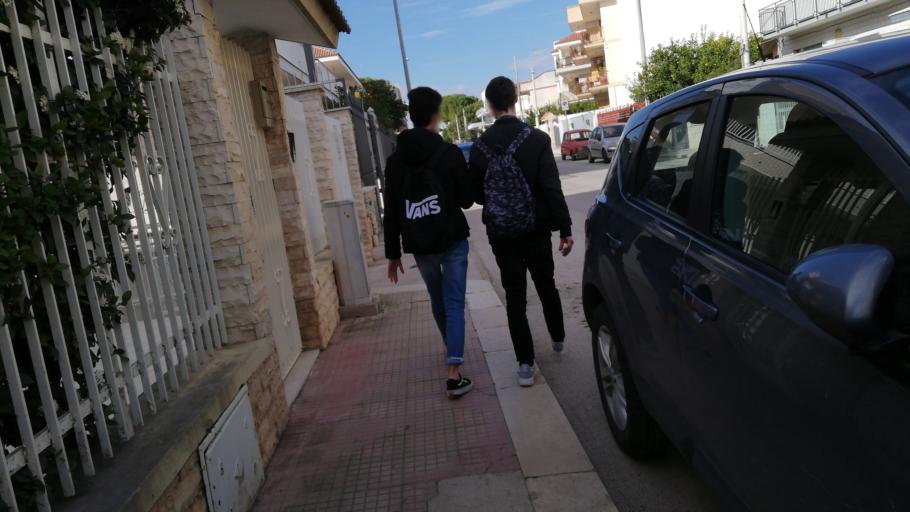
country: IT
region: Apulia
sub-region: Provincia di Bari
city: Bitonto
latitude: 41.1104
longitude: 16.6807
